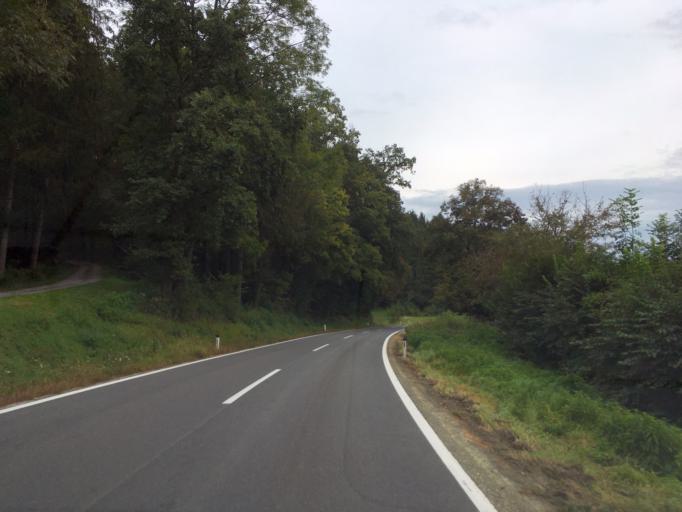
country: AT
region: Styria
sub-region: Politischer Bezirk Graz-Umgebung
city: Eggersdorf bei Graz
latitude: 47.1033
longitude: 15.5922
